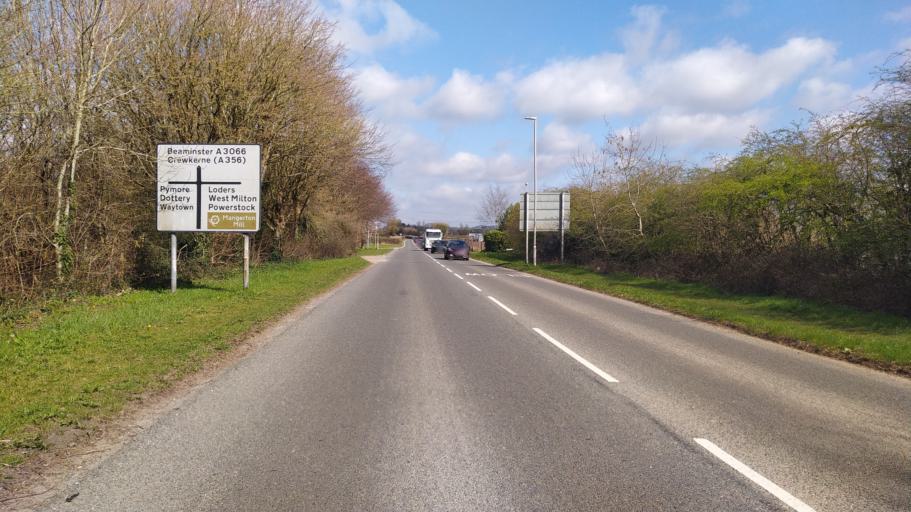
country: GB
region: England
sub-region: Dorset
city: Bridport
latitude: 50.7488
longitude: -2.7421
